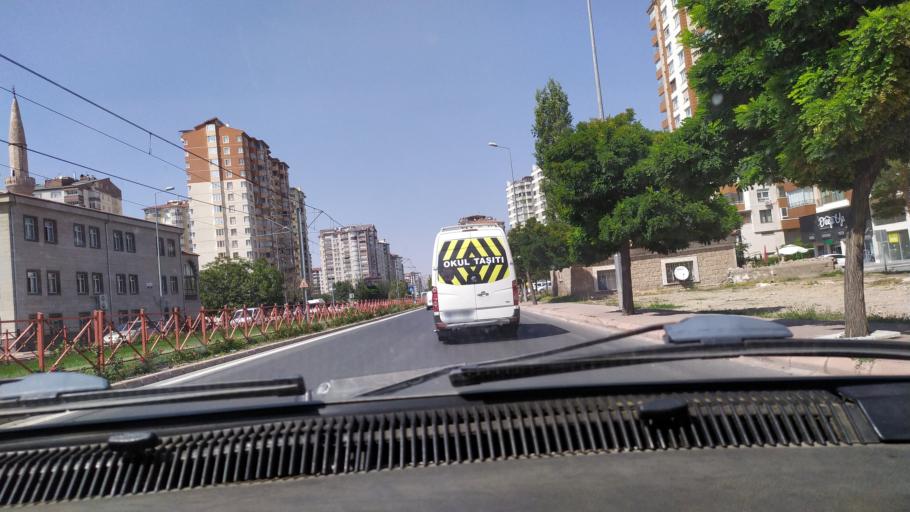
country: TR
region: Kayseri
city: Kayseri
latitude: 38.7250
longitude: 35.5270
